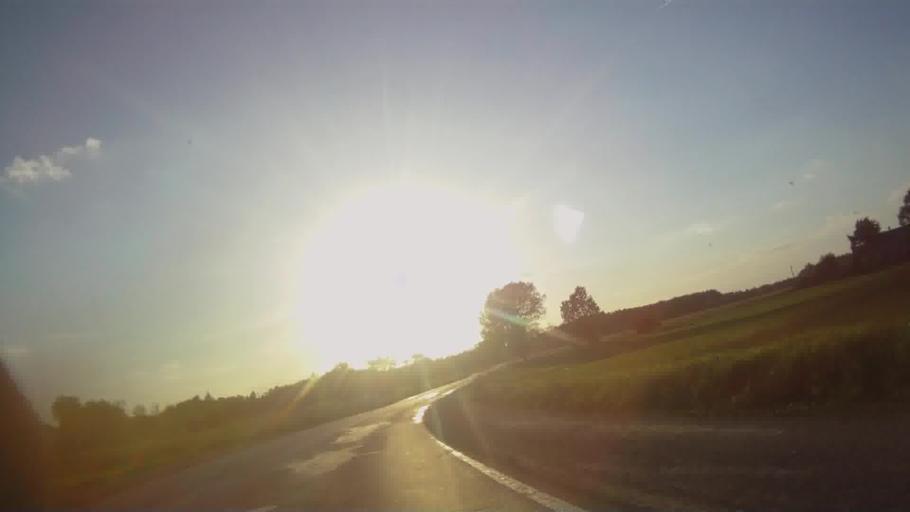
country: LV
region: Jekabpils Rajons
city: Jekabpils
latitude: 56.5242
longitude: 25.8376
